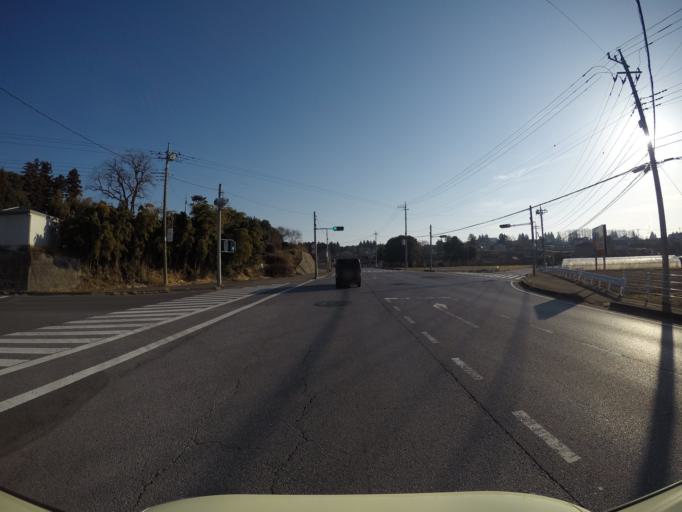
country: JP
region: Tochigi
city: Utsunomiya-shi
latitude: 36.5488
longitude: 139.9697
